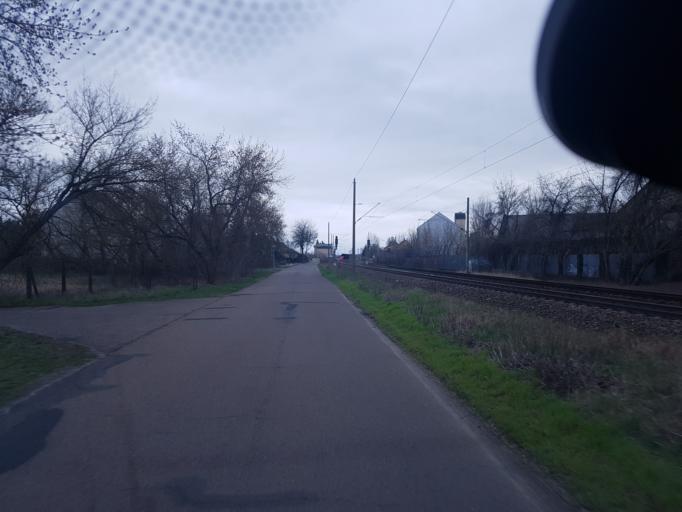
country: DE
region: Brandenburg
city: Eisenhuettenstadt
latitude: 52.1518
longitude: 14.6592
